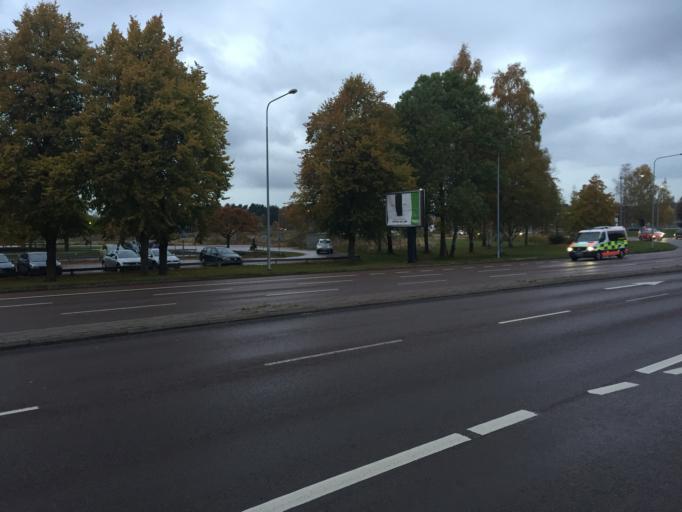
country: SE
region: Vaermland
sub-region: Karlstads Kommun
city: Karlstad
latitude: 59.3826
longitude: 13.4887
